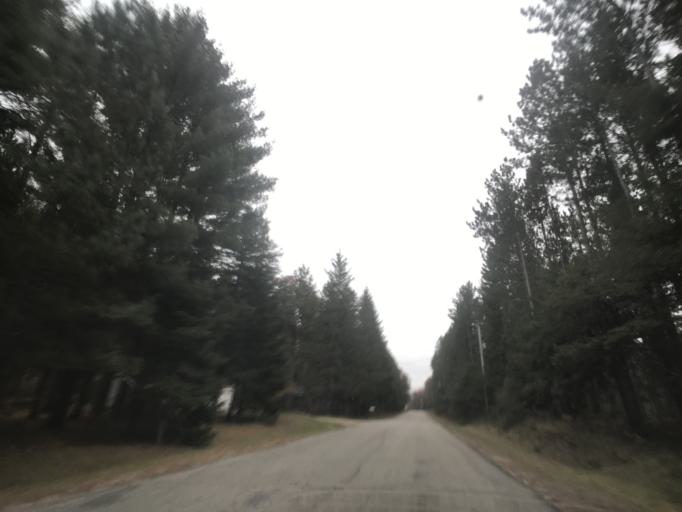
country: US
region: Wisconsin
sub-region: Oconto County
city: Gillett
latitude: 45.3035
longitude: -88.2651
